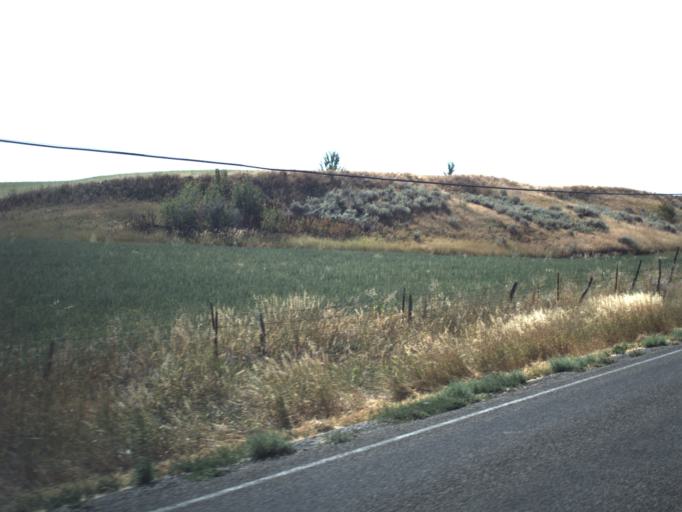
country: US
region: Utah
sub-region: Cache County
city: Hyrum
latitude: 41.5932
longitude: -111.8368
